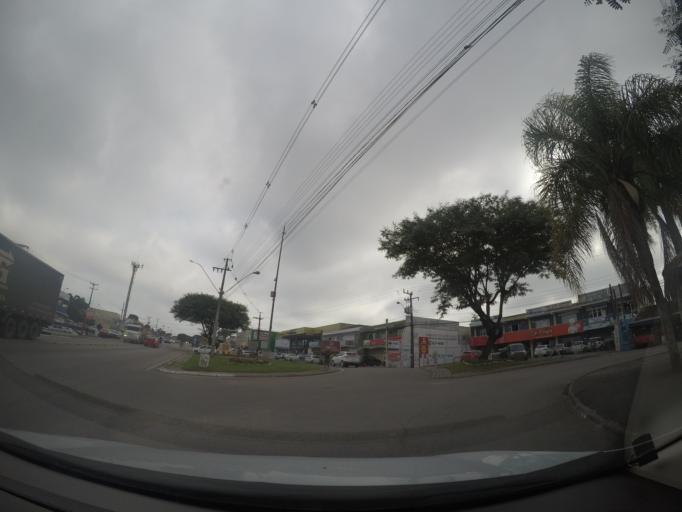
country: BR
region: Parana
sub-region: Colombo
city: Colombo
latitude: -25.3528
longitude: -49.2193
